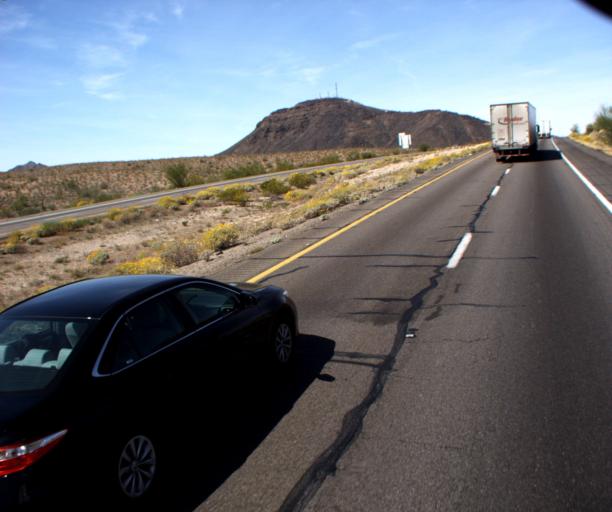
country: US
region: Arizona
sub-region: La Paz County
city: Quartzsite
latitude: 33.6655
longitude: -114.0337
